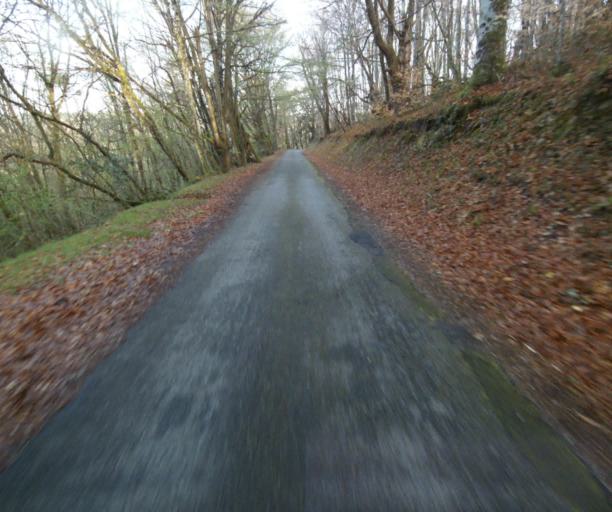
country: FR
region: Limousin
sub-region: Departement de la Correze
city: Correze
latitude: 45.2950
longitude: 1.8478
